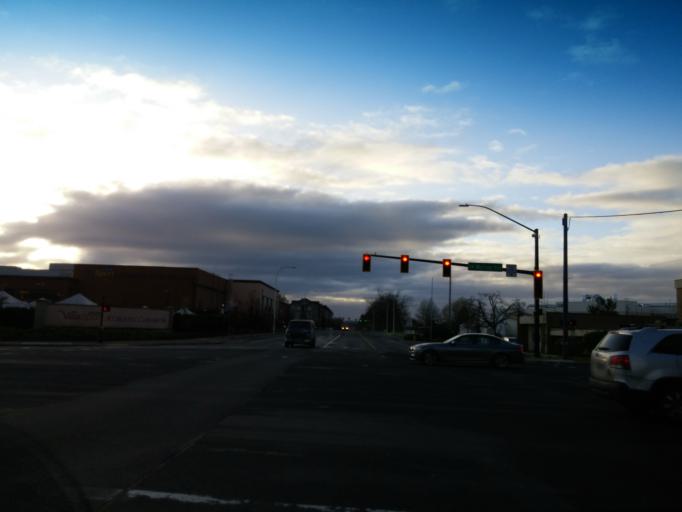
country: US
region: Oregon
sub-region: Washington County
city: Cedar Mill
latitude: 45.5040
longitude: -122.8269
